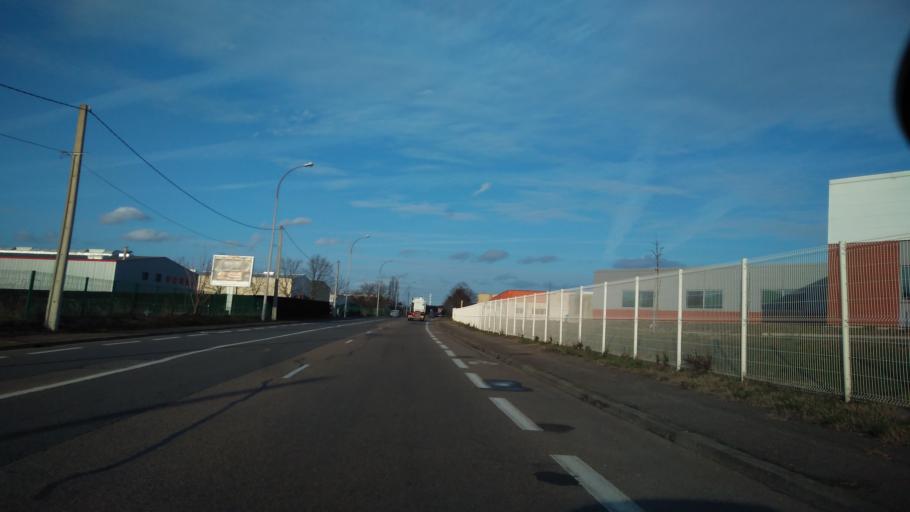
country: FR
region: Rhone-Alpes
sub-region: Departement du Rhone
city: Corbas
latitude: 45.6729
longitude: 4.9133
